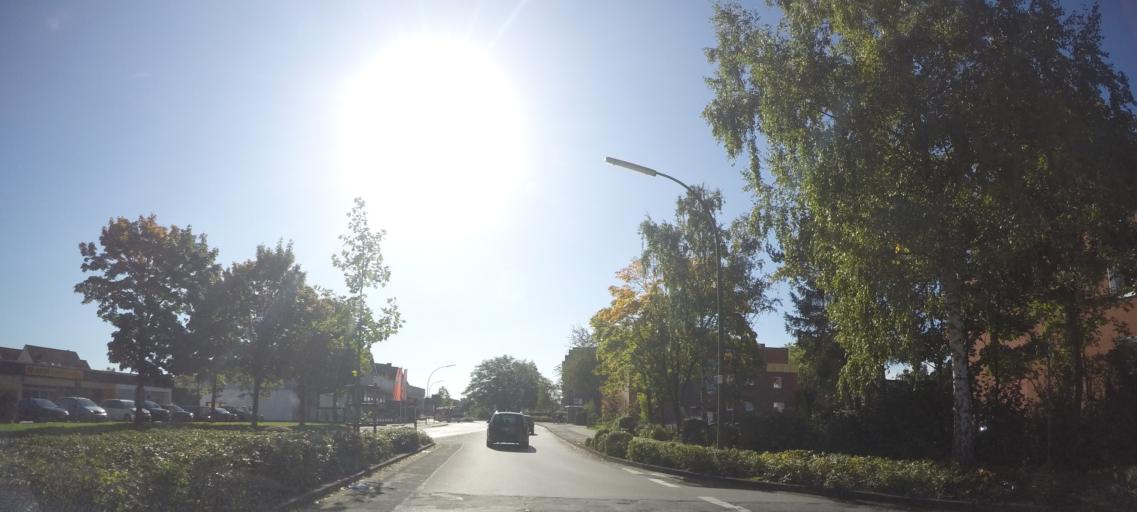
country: DE
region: North Rhine-Westphalia
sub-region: Regierungsbezirk Arnsberg
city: Hamm
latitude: 51.6899
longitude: 7.8827
